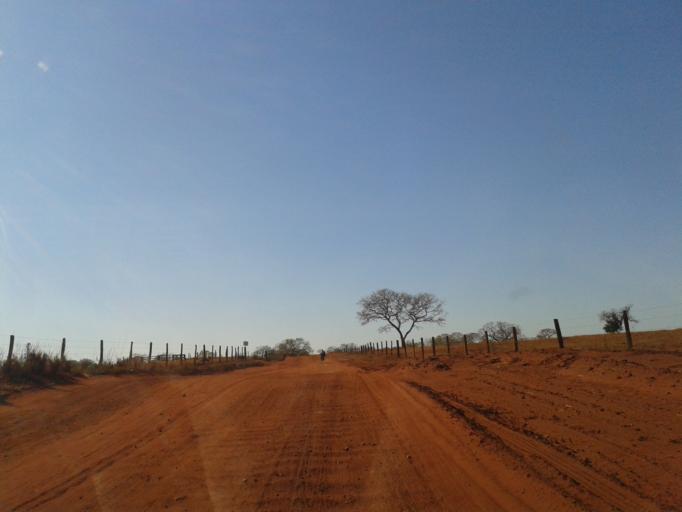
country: BR
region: Minas Gerais
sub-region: Ituiutaba
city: Ituiutaba
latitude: -18.9799
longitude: -49.4064
